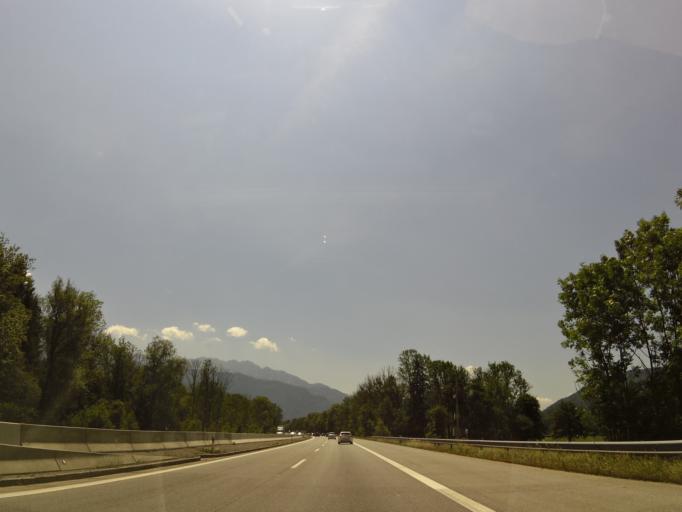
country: DE
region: Bavaria
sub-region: Upper Bavaria
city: Oberaudorf
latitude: 47.6589
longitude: 12.1838
